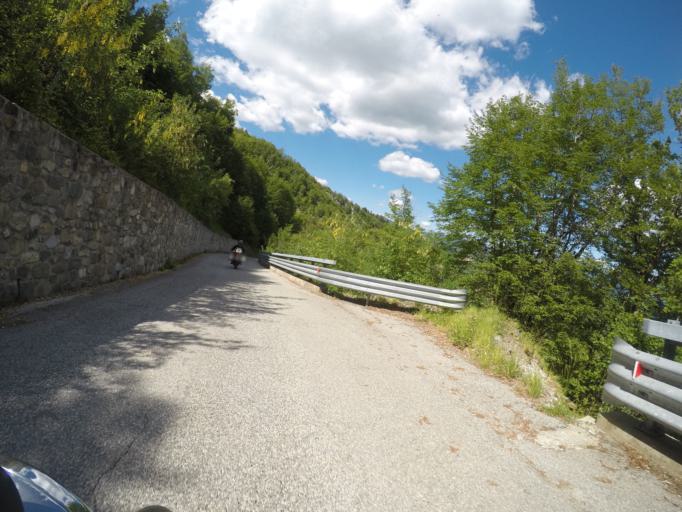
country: IT
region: Tuscany
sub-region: Provincia di Lucca
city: Minucciano
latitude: 44.1579
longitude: 10.2001
